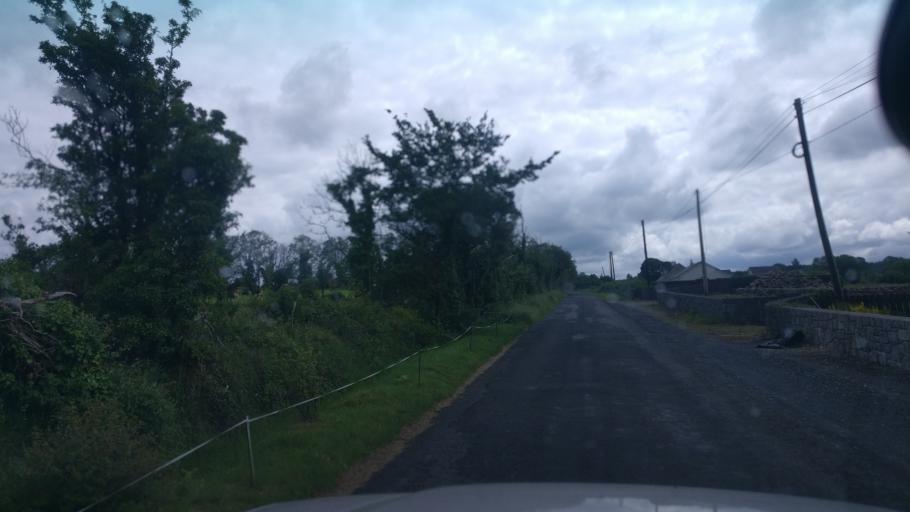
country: IE
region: Connaught
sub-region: County Galway
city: Loughrea
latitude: 53.1613
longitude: -8.5723
